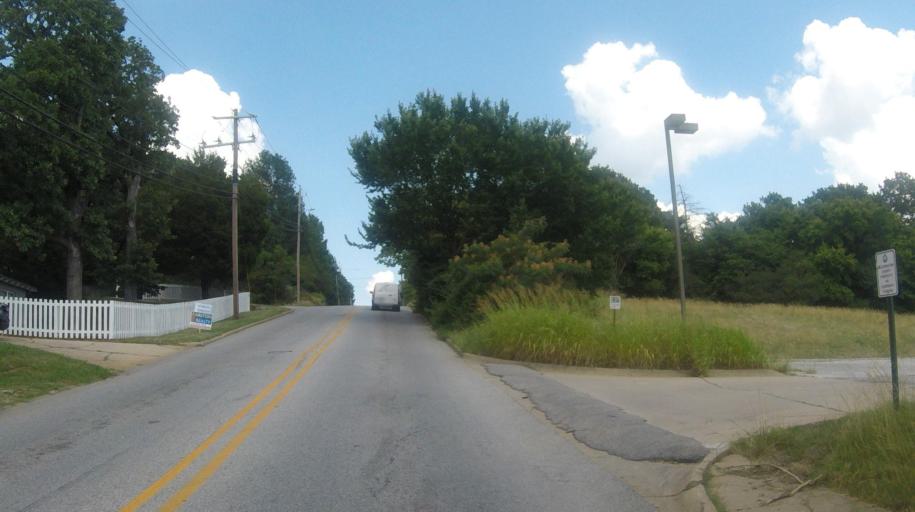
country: US
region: Arkansas
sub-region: Washington County
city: Fayetteville
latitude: 36.0772
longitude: -94.1566
